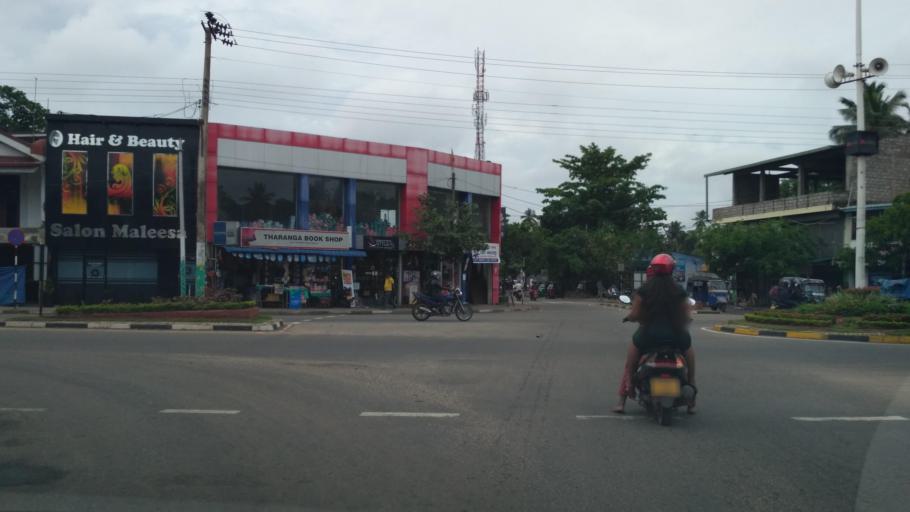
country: LK
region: North Western
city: Kuliyapitiya
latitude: 7.3285
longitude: 80.0243
